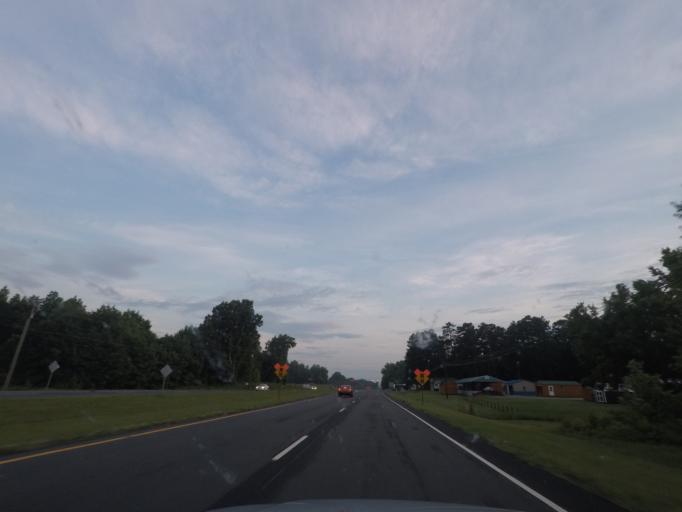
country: US
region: North Carolina
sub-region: Person County
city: Roxboro
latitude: 36.2814
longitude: -78.9548
